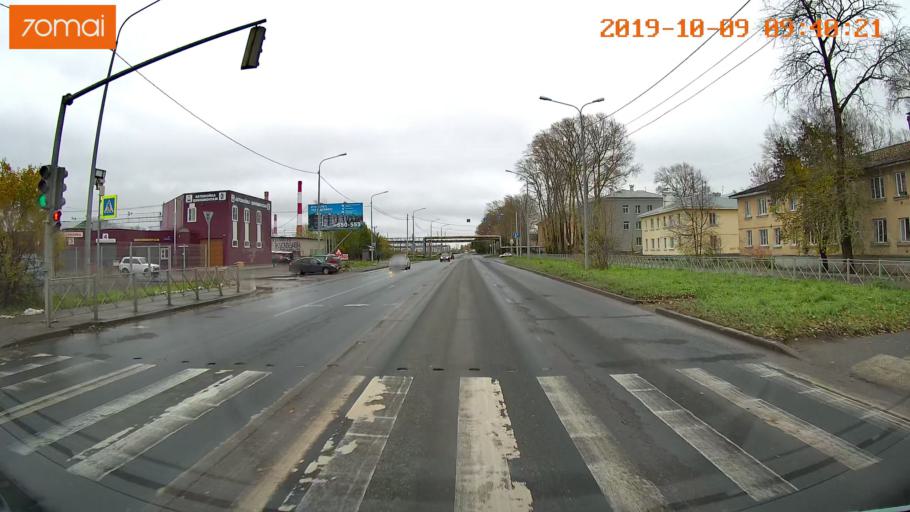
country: RU
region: Vologda
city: Vologda
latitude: 59.1954
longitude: 39.9248
